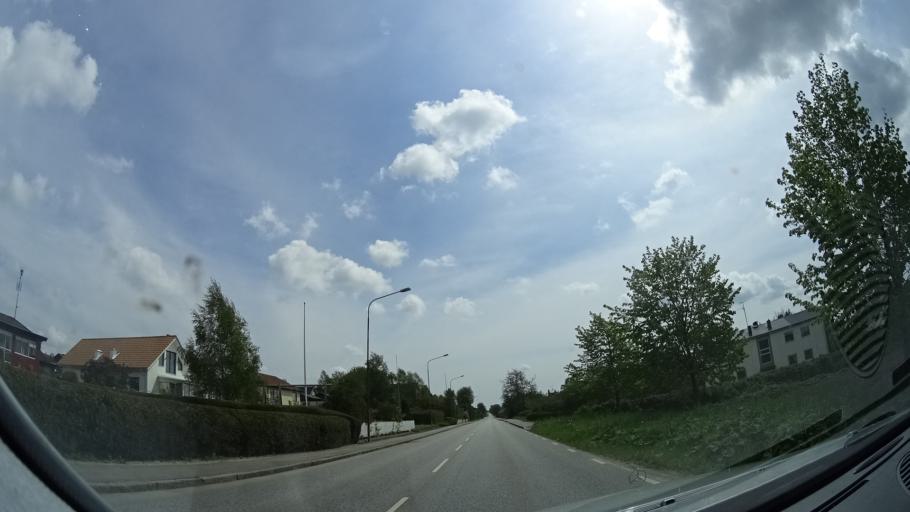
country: SE
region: Skane
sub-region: Hoors Kommun
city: Loberod
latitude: 55.7185
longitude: 13.5217
